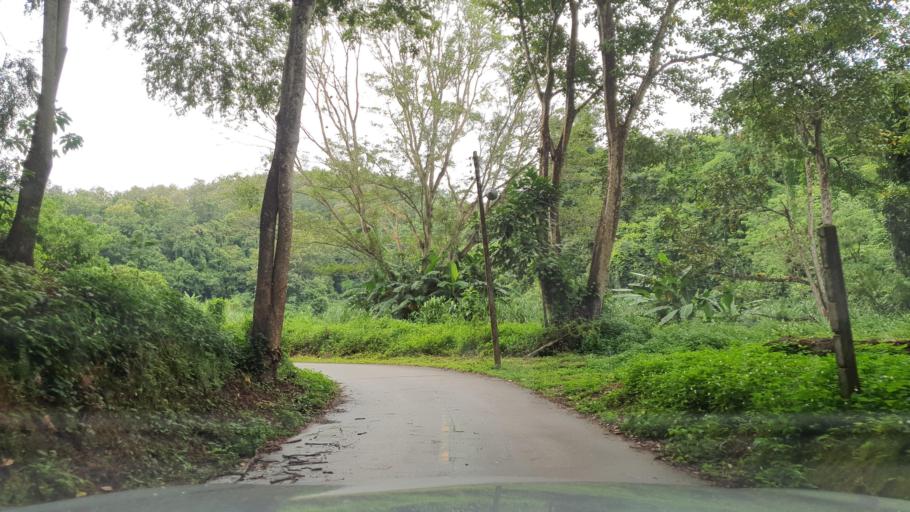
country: TH
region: Chiang Mai
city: Mae Taeng
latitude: 19.2002
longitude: 98.9389
